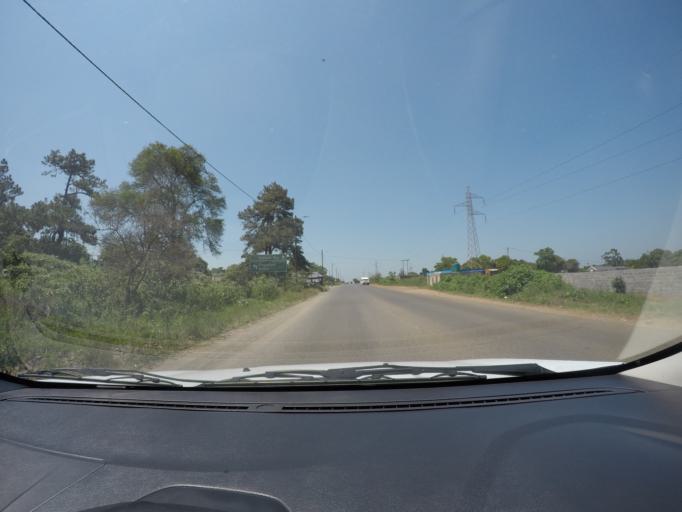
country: ZA
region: KwaZulu-Natal
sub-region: uThungulu District Municipality
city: eSikhawini
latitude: -28.8418
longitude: 31.9346
